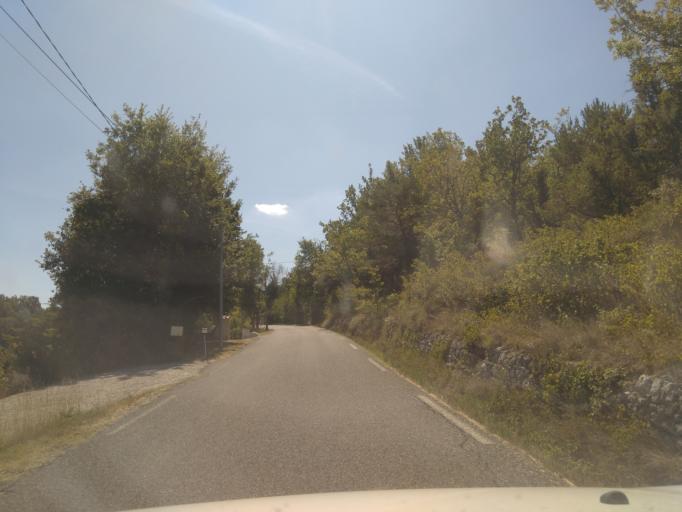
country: FR
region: Provence-Alpes-Cote d'Azur
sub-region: Departement du Var
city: Regusse
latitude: 43.7081
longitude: 6.0884
